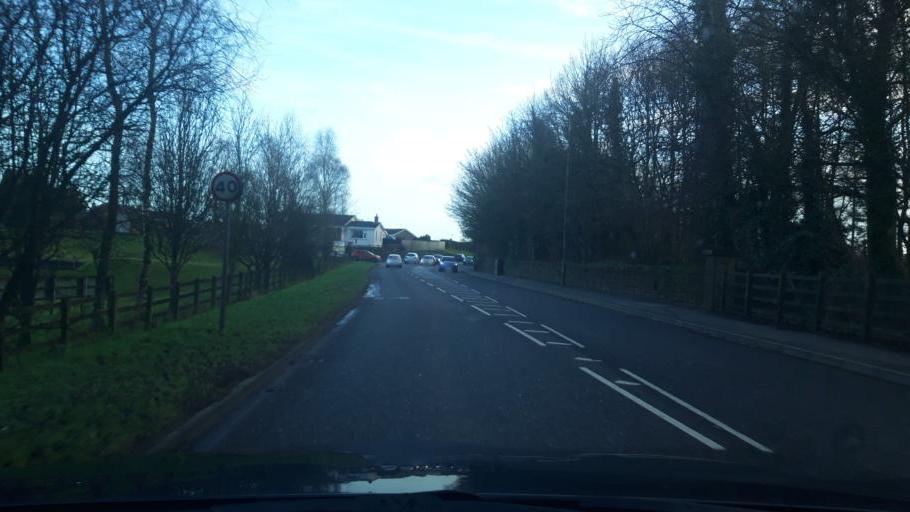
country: GB
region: Northern Ireland
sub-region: Dungannon District
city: Dungannon
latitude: 54.4917
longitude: -6.7507
